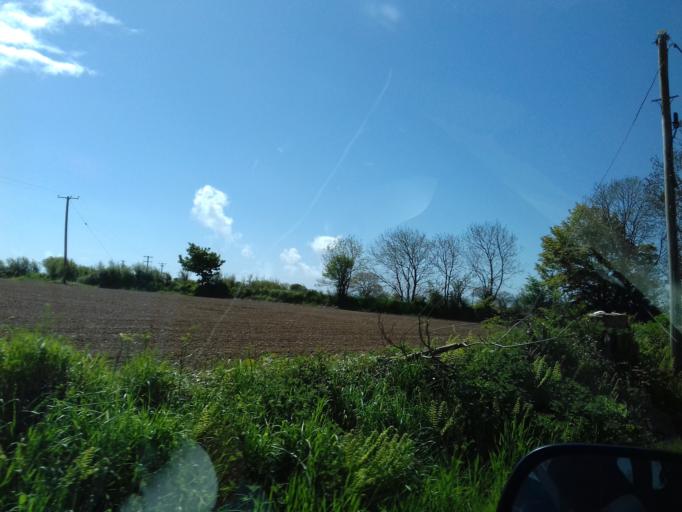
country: IE
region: Munster
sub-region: Waterford
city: Dunmore East
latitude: 52.2324
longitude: -6.8615
